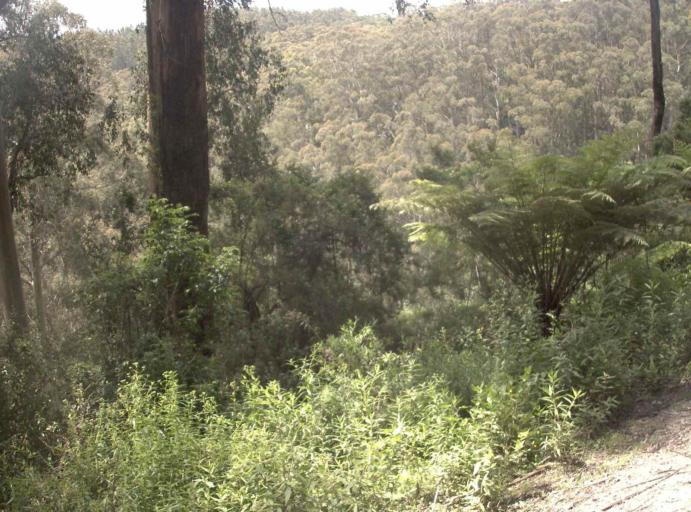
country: AU
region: Victoria
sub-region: Latrobe
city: Morwell
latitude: -38.4386
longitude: 146.5249
